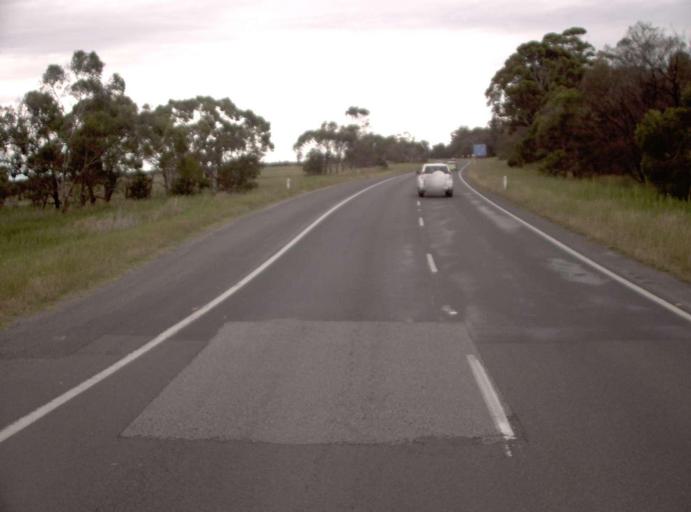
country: AU
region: Victoria
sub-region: Casey
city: Tooradin
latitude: -38.2137
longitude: 145.4148
